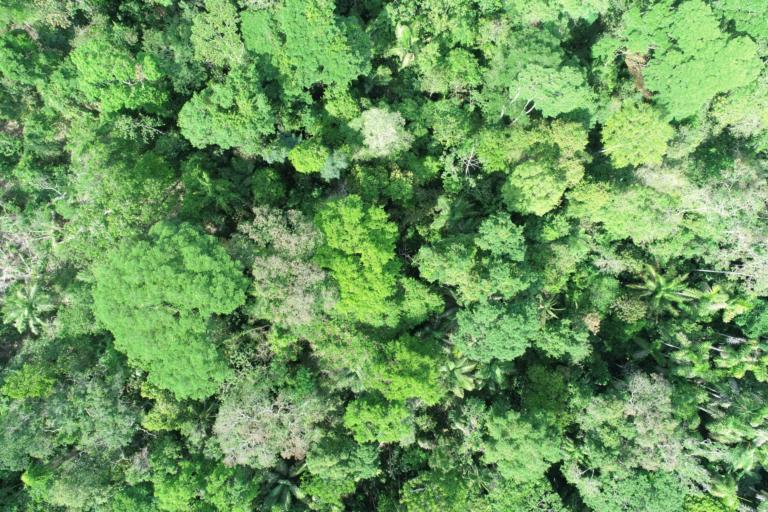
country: BO
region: El Beni
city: San Borja
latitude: -14.7469
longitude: -67.1708
